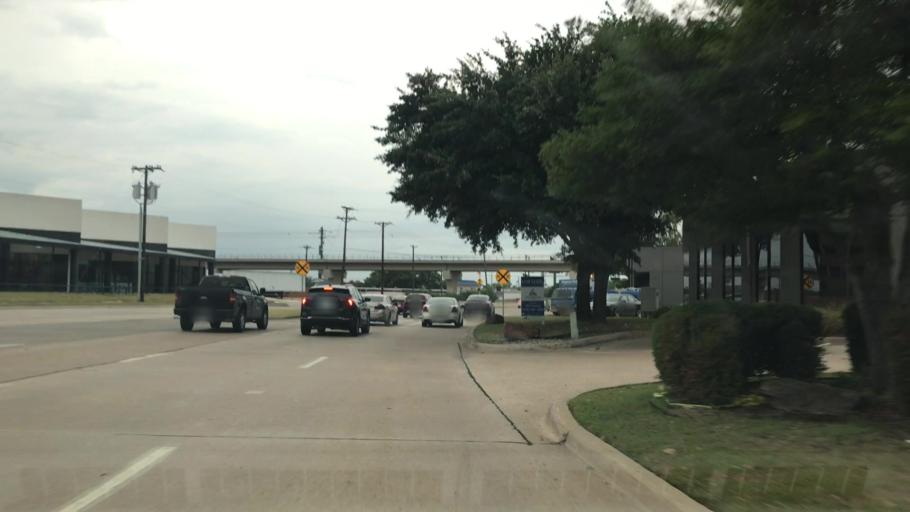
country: US
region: Texas
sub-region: Dallas County
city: Carrollton
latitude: 32.9654
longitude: -96.9136
